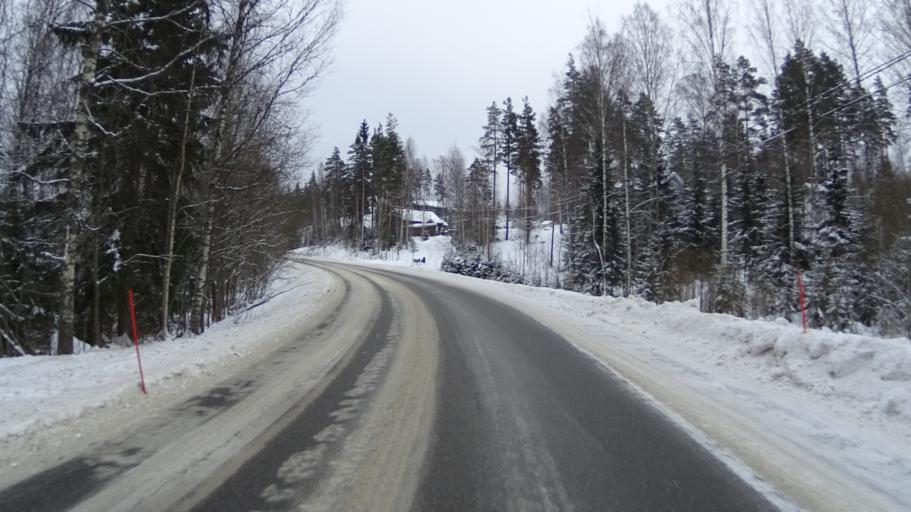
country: FI
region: Uusimaa
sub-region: Helsinki
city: Karkkila
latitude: 60.5053
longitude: 24.1451
